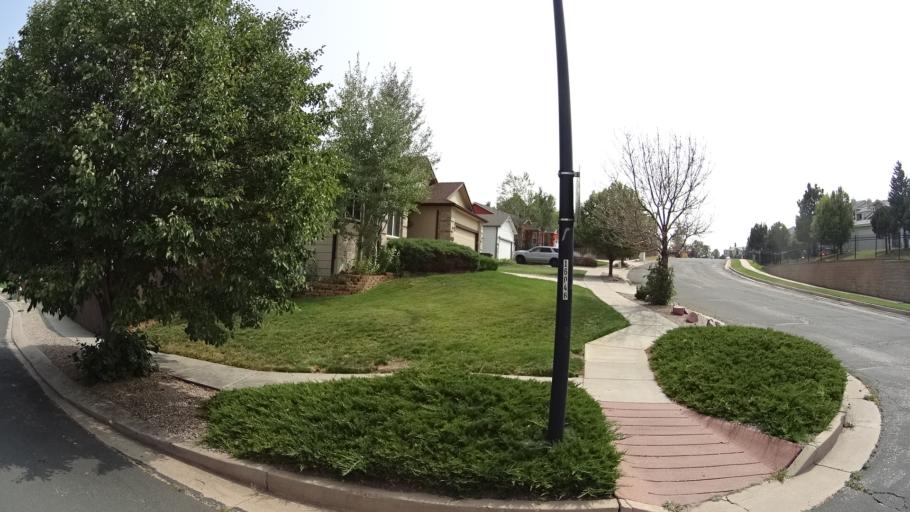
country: US
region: Colorado
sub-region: El Paso County
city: Cimarron Hills
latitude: 38.9247
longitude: -104.7365
